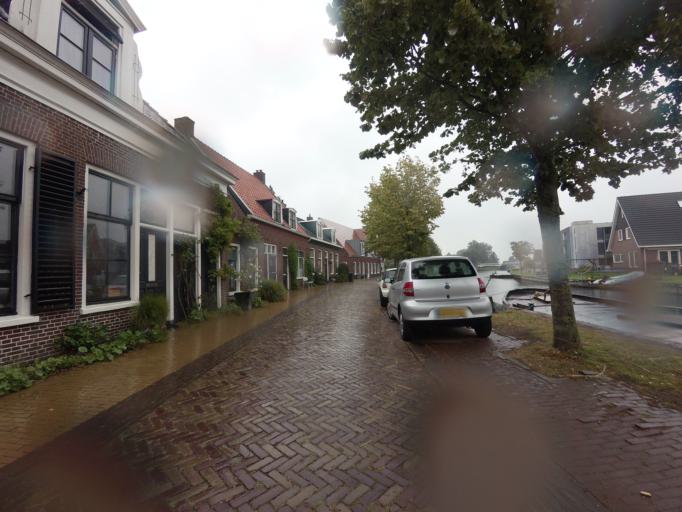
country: NL
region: Friesland
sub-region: Gemeente Boarnsterhim
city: Aldeboarn
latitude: 53.0490
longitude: 5.8968
